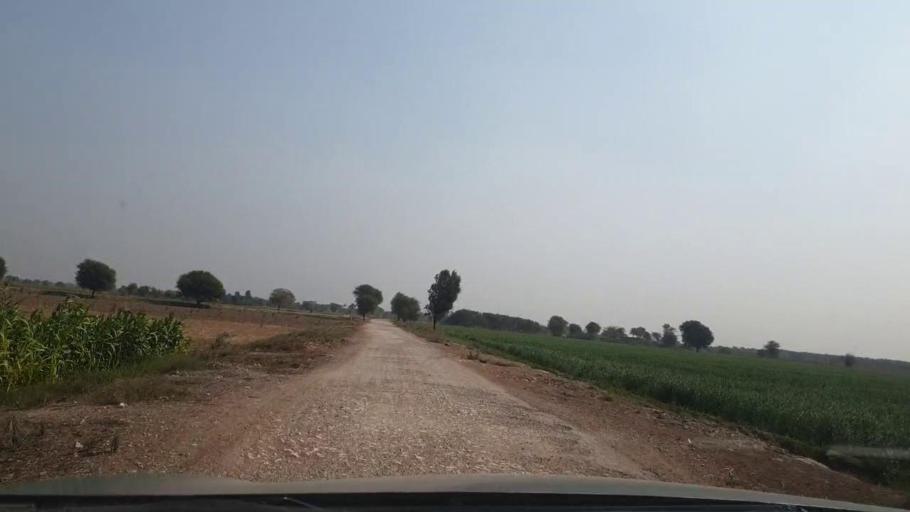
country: PK
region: Sindh
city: Tando Allahyar
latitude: 25.5629
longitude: 68.8238
